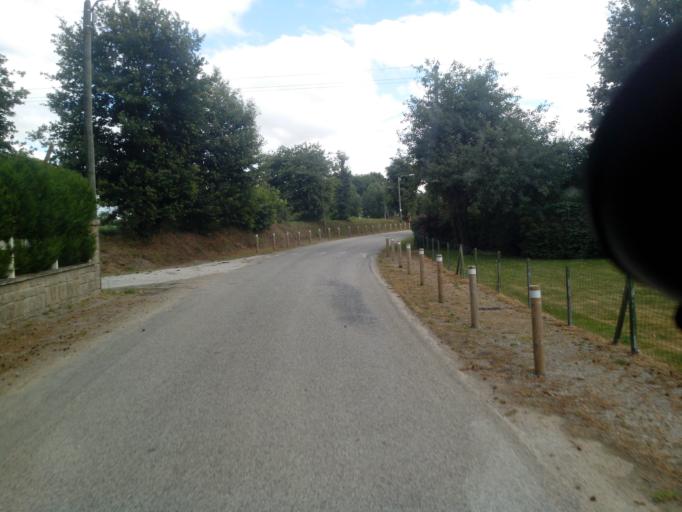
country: FR
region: Brittany
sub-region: Departement du Morbihan
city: Meneac
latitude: 48.1358
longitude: -2.4558
